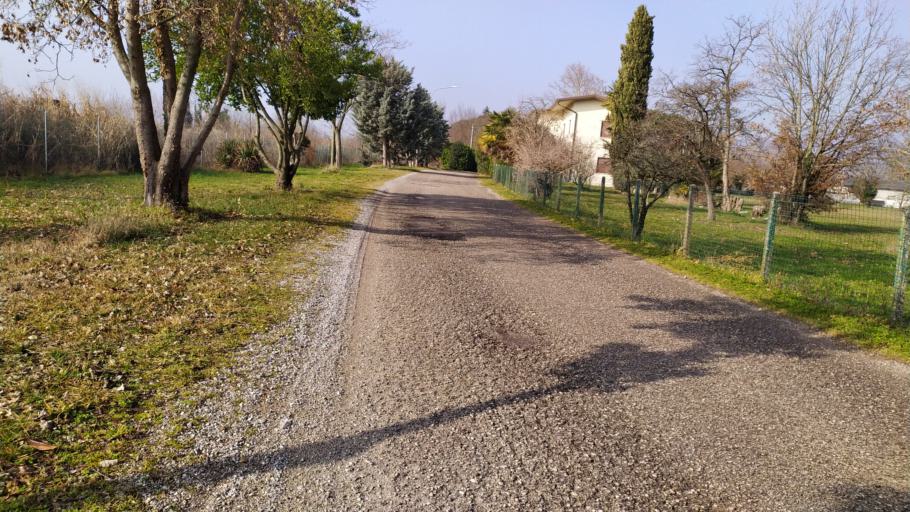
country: IT
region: Veneto
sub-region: Provincia di Treviso
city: Godega
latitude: 45.9393
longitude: 12.3828
